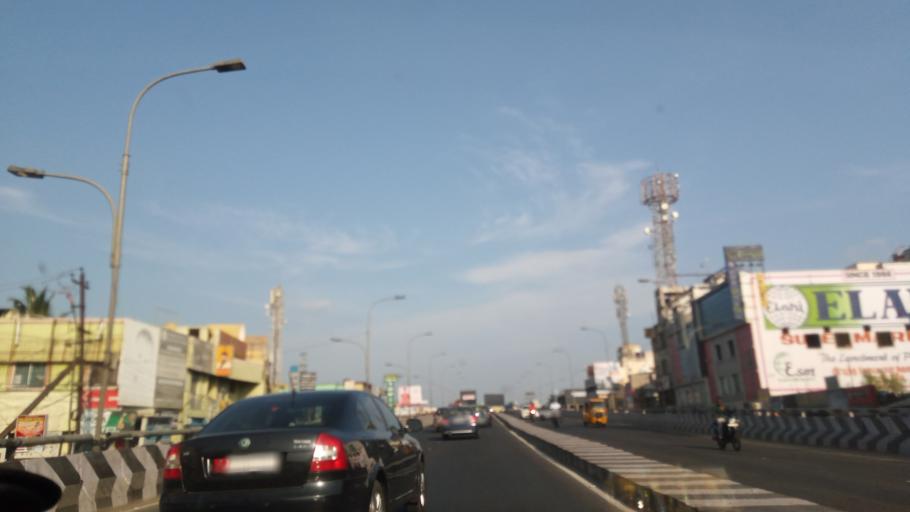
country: IN
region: Tamil Nadu
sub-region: Thiruvallur
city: Porur
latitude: 13.0356
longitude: 80.1543
